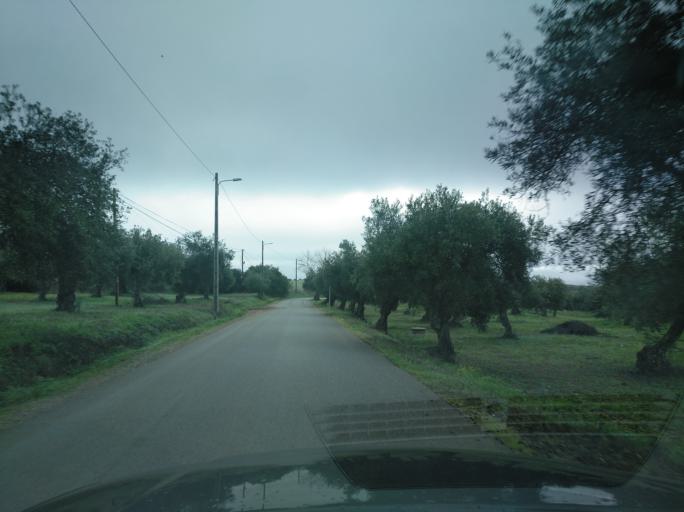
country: PT
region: Portalegre
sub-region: Elvas
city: Elvas
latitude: 38.8636
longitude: -7.1642
